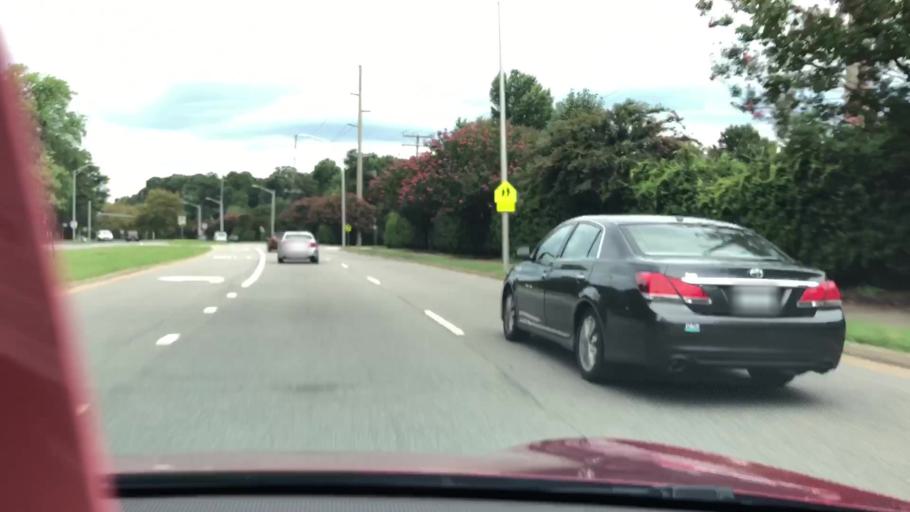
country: US
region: Virginia
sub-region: City of Virginia Beach
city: Virginia Beach
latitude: 36.8884
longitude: -76.0504
